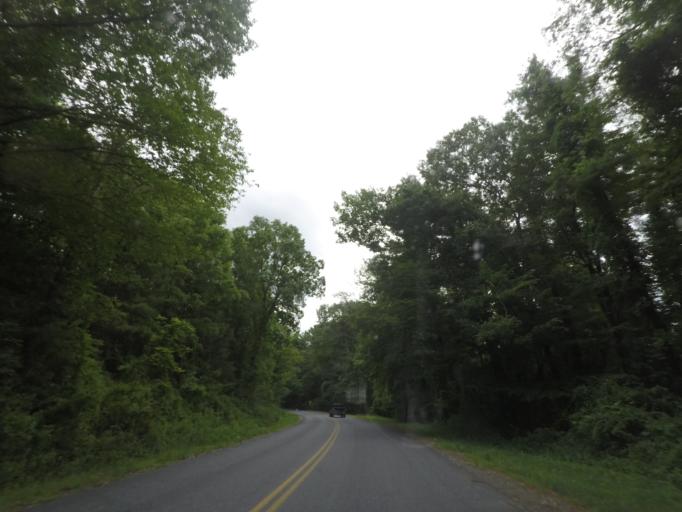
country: US
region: New York
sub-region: Saratoga County
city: Stillwater
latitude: 42.8525
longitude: -73.5450
